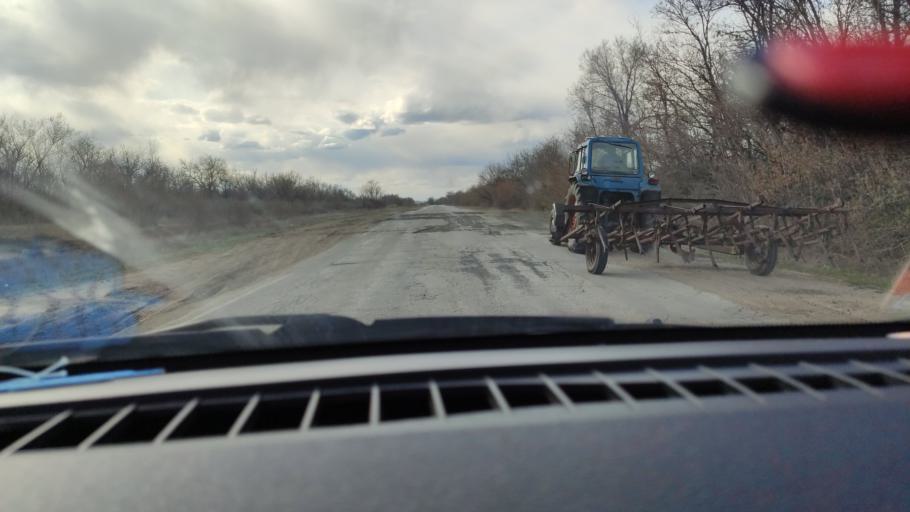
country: RU
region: Saratov
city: Rovnoye
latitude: 51.0430
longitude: 46.0628
